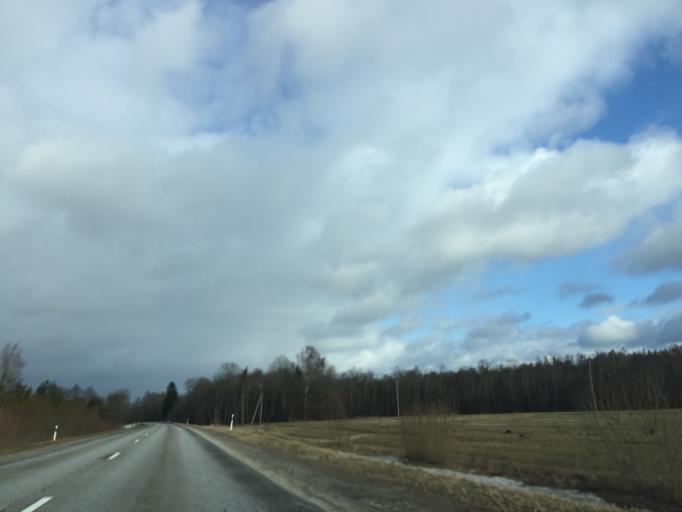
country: LV
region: Aloja
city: Staicele
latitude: 57.8826
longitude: 24.6008
